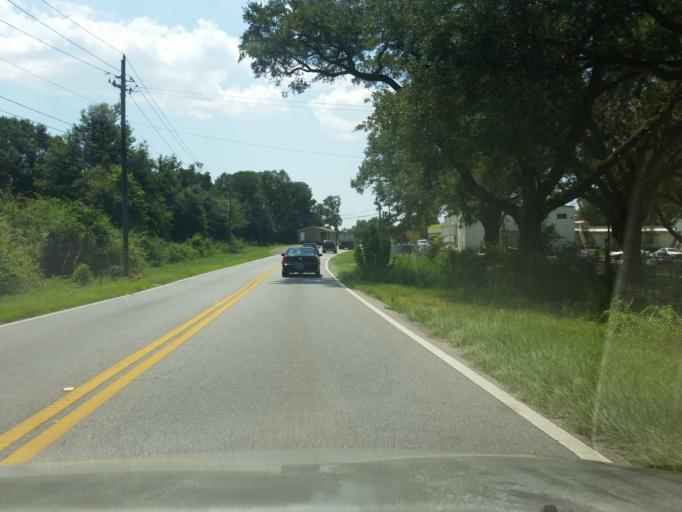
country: US
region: Florida
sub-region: Escambia County
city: Gonzalez
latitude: 30.5662
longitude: -87.2876
